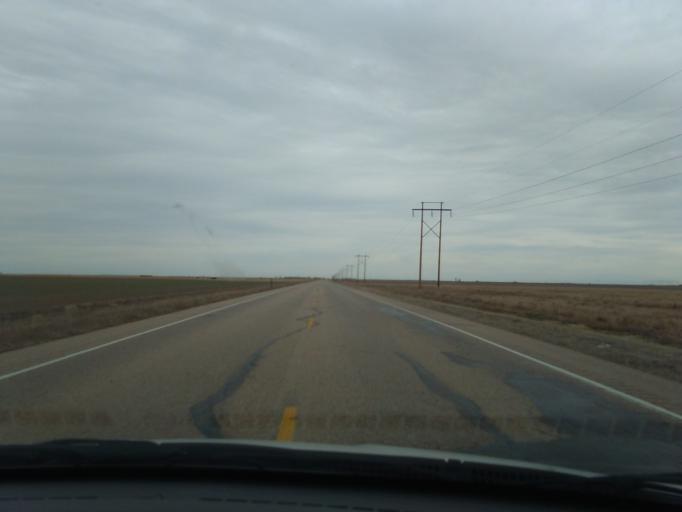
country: US
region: Colorado
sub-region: Yuma County
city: Yuma
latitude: 40.1491
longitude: -102.9136
